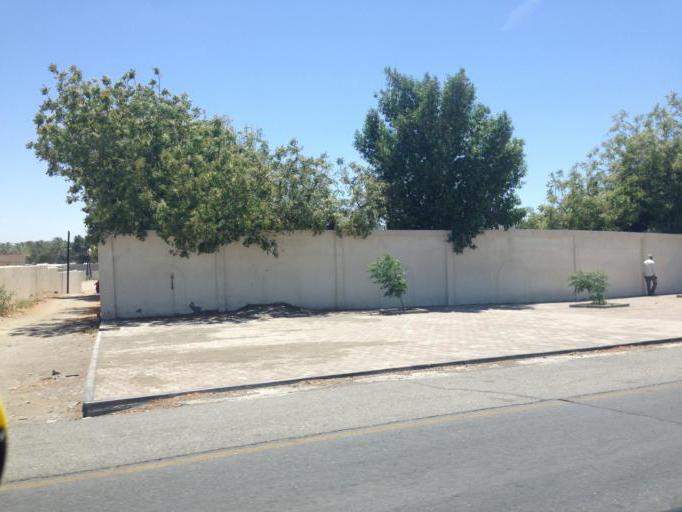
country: OM
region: Muhafazat Masqat
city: As Sib al Jadidah
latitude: 23.6637
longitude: 58.2074
